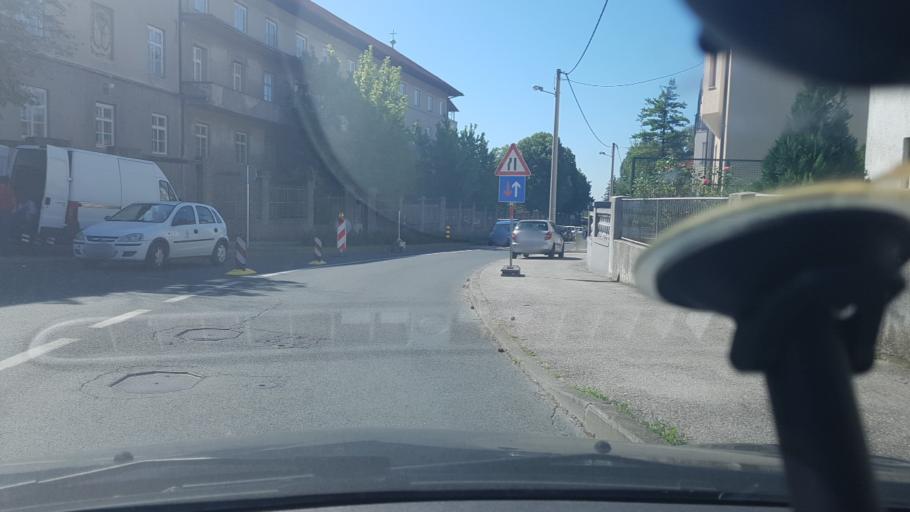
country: HR
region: Grad Zagreb
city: Zagreb
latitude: 45.8236
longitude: 15.9856
